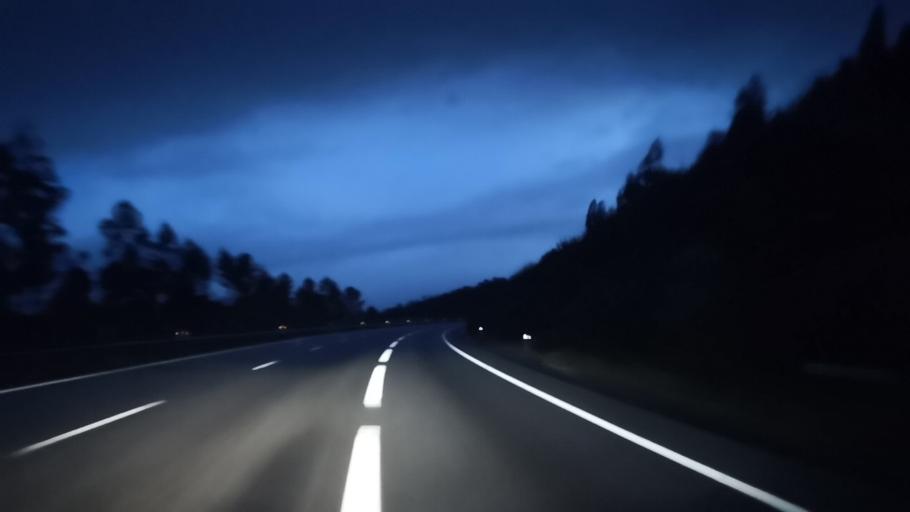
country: PT
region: Braga
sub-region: Guimaraes
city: Brito
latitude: 41.4743
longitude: -8.3871
